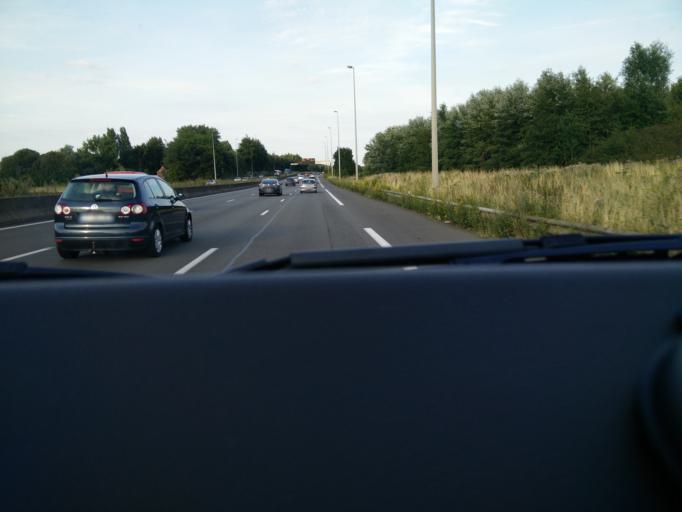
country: FR
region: Nord-Pas-de-Calais
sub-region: Departement du Nord
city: Haubourdin
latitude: 50.6183
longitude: 3.0006
